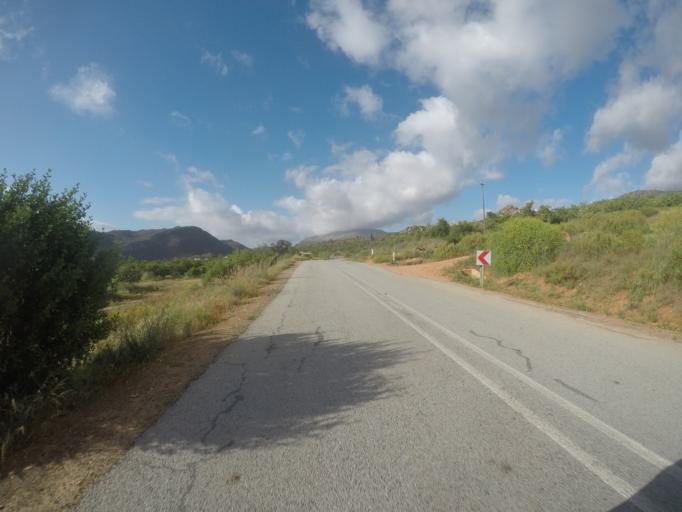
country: ZA
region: Western Cape
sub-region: West Coast District Municipality
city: Clanwilliam
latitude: -32.4336
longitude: 18.9394
